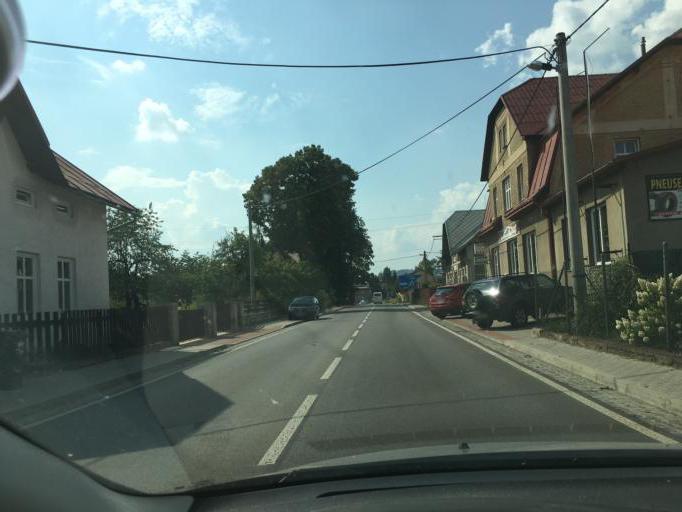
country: CZ
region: Kralovehradecky
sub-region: Okres Trutnov
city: Vrchlabi
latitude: 50.6194
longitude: 15.6589
